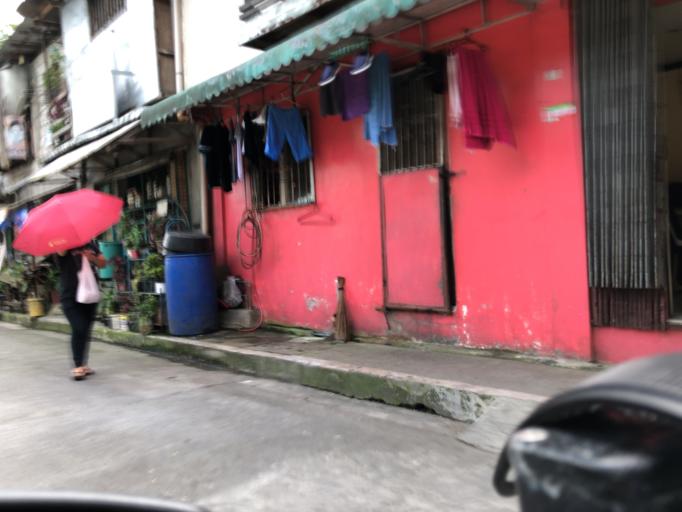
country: PH
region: Central Luzon
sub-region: Province of Bulacan
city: San Jose del Monte
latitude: 14.7580
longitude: 121.0546
